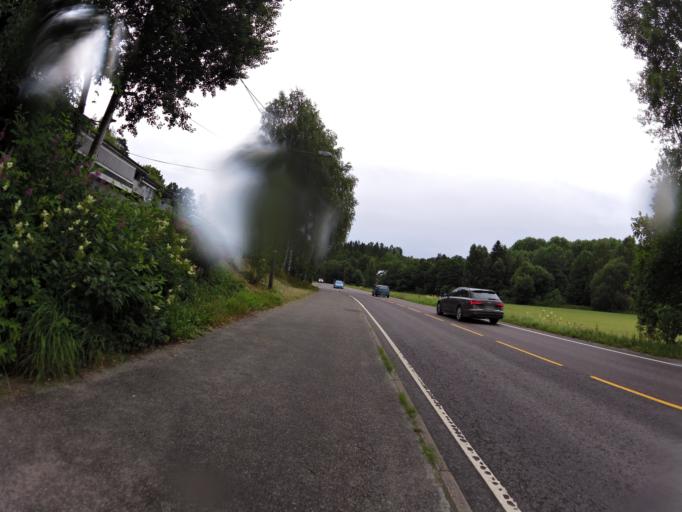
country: NO
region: Ostfold
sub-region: Moss
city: Moss
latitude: 59.4707
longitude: 10.6905
